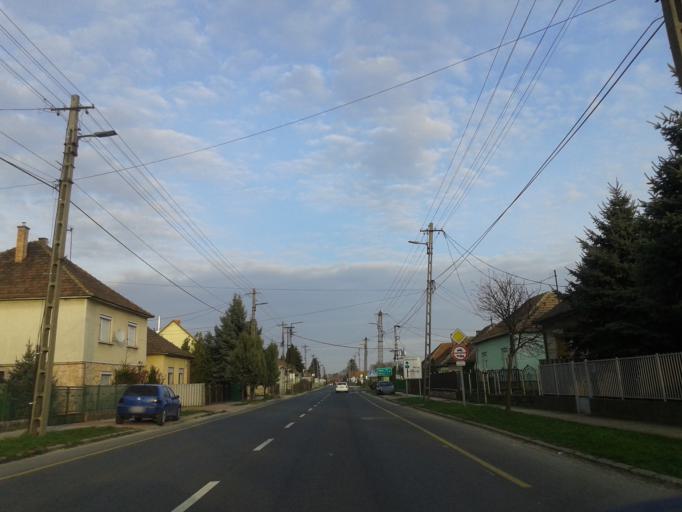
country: HU
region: Komarom-Esztergom
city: Komarom
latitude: 47.7361
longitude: 18.1545
